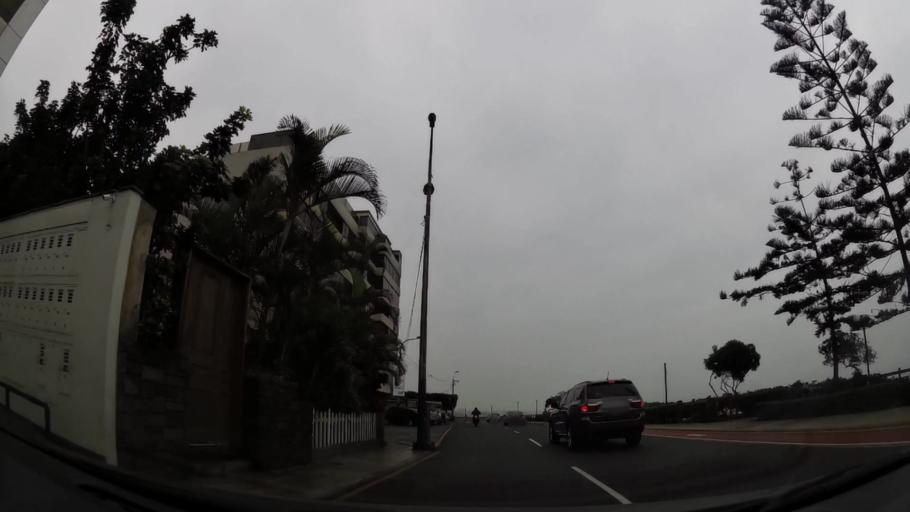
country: PE
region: Lima
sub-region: Lima
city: San Isidro
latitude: -12.1293
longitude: -77.0346
